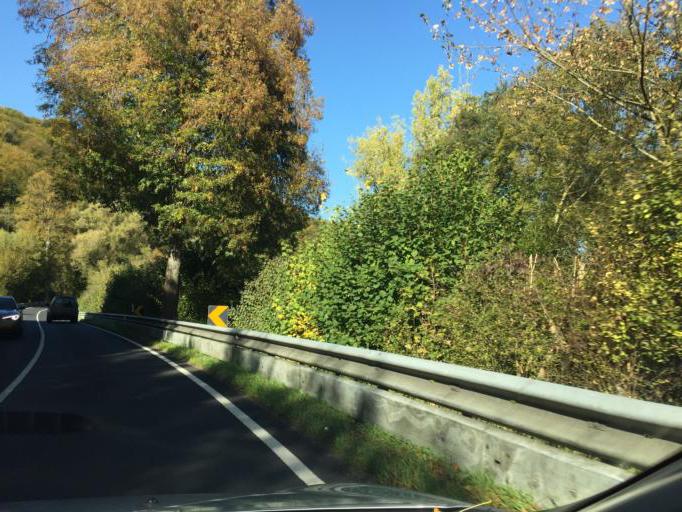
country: LU
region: Luxembourg
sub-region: Canton de Capellen
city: Kopstal
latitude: 49.6741
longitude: 6.0804
